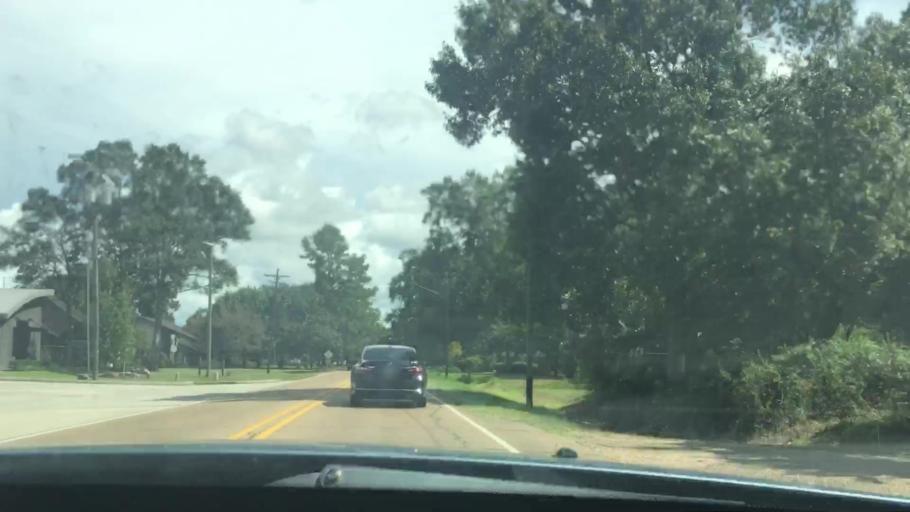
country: US
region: Louisiana
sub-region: East Baton Rouge Parish
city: Westminster
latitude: 30.4496
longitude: -91.0705
